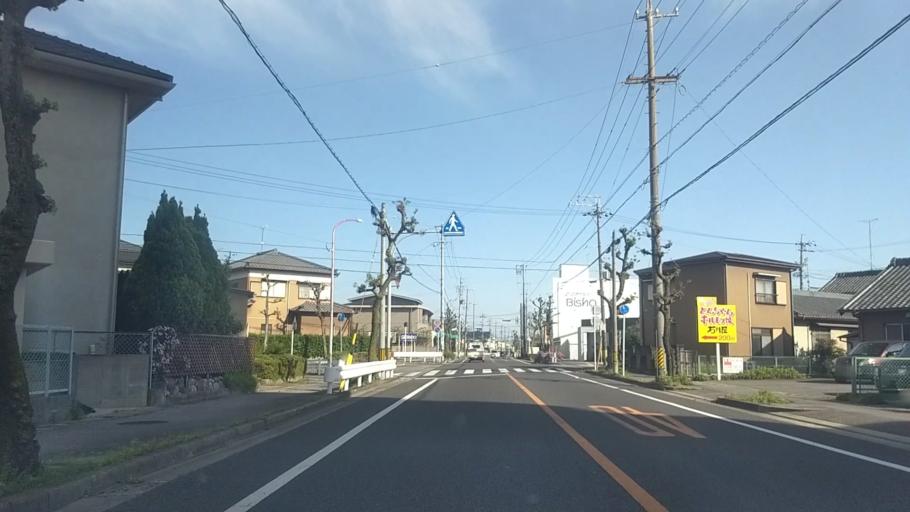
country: JP
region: Aichi
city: Anjo
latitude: 34.9520
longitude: 137.0934
